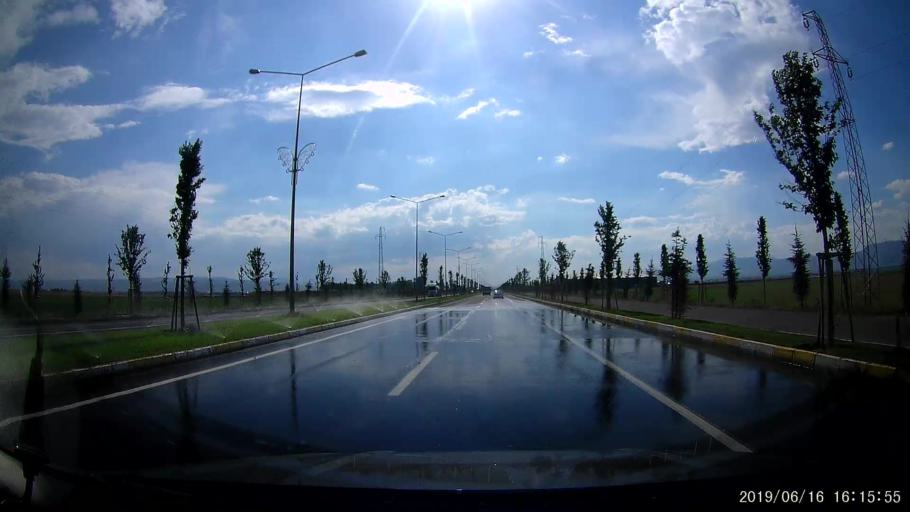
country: TR
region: Erzurum
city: Erzurum
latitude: 39.9624
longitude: 41.2162
